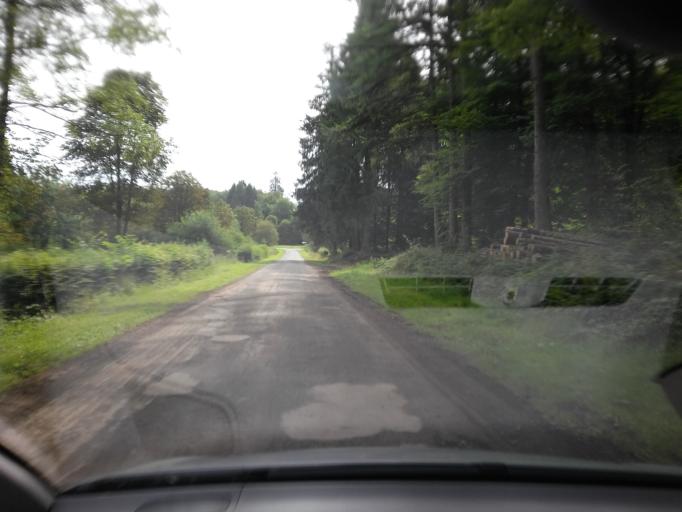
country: BE
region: Wallonia
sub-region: Province du Luxembourg
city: Chiny
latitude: 49.7526
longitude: 5.3030
